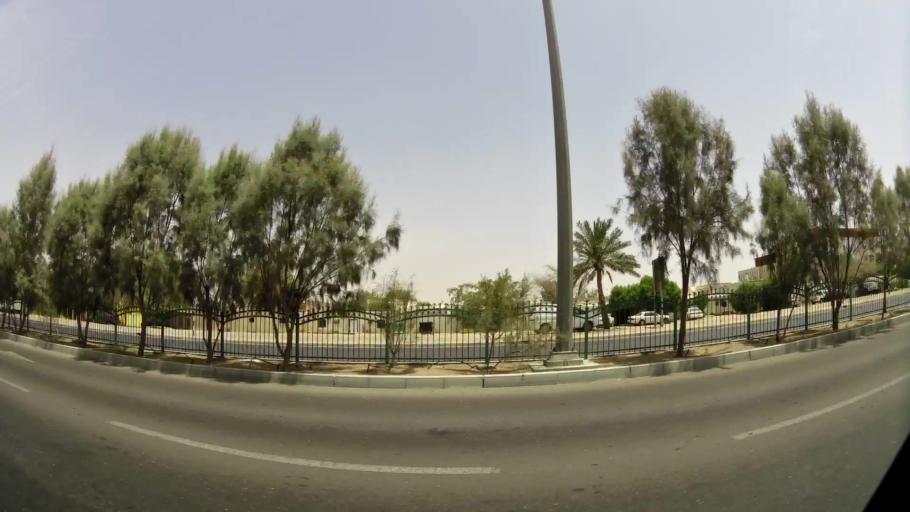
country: AE
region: Abu Dhabi
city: Al Ain
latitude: 24.2053
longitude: 55.7573
